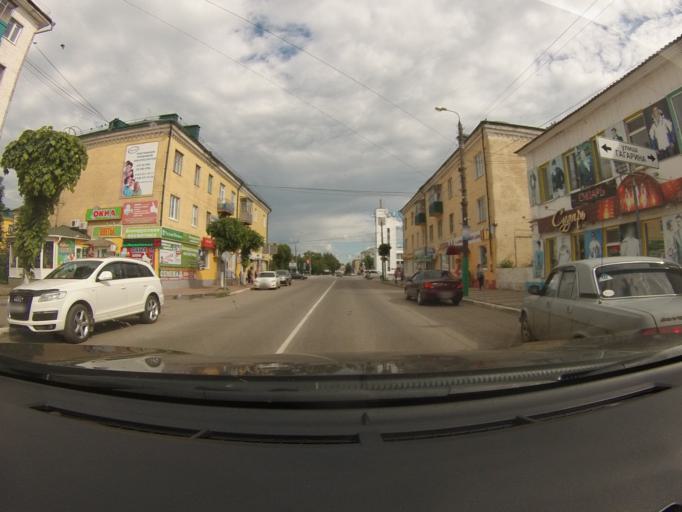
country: RU
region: Orjol
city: Mtsensk
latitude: 53.2793
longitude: 36.5741
